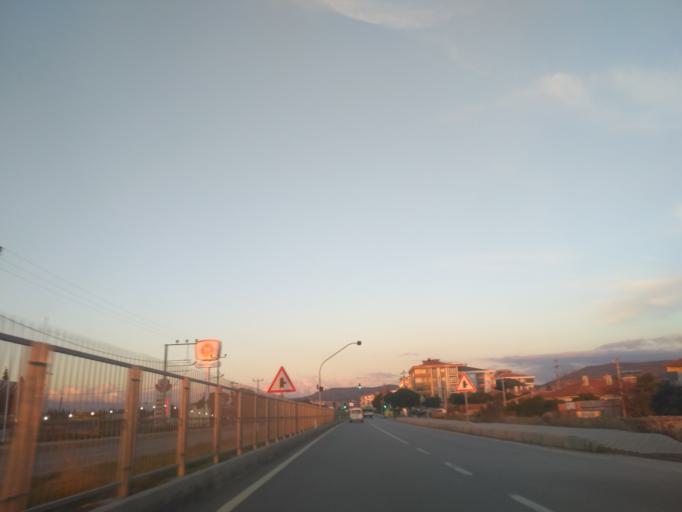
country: TR
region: Balikesir
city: Emrutabat
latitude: 39.3913
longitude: 26.8387
